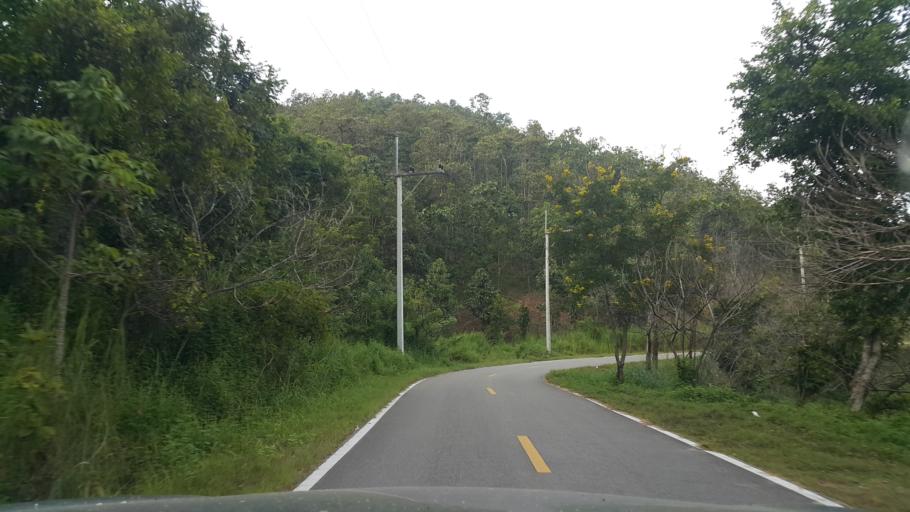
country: TH
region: Chiang Mai
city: San Sai
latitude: 18.9389
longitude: 99.0609
